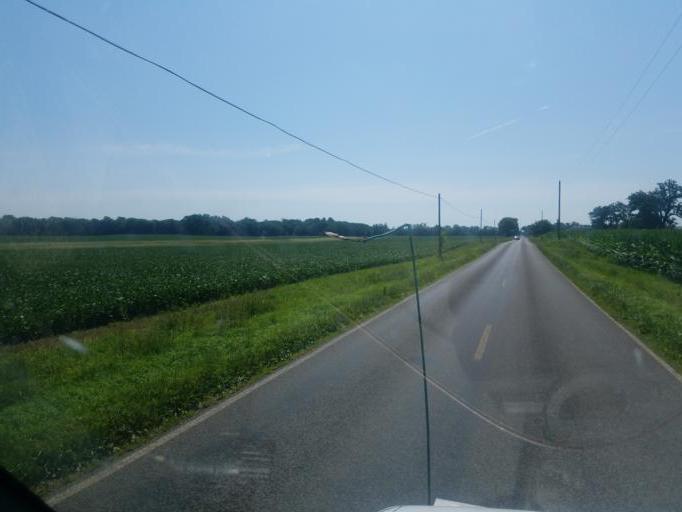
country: US
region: Ohio
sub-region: Champaign County
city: North Lewisburg
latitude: 40.2160
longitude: -83.5087
